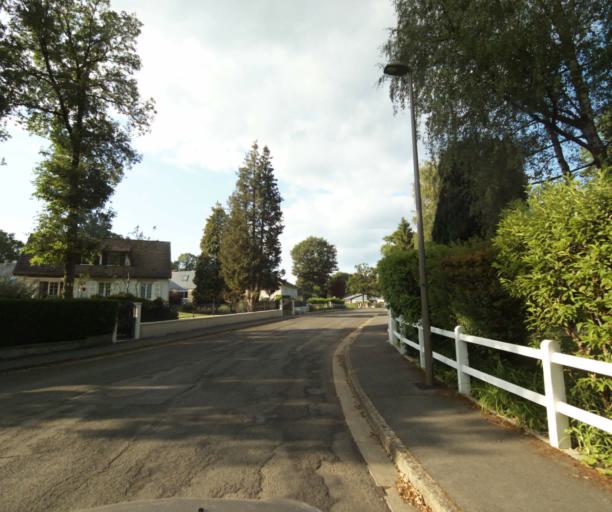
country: FR
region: Champagne-Ardenne
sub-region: Departement des Ardennes
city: Charleville-Mezieres
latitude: 49.7968
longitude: 4.7145
